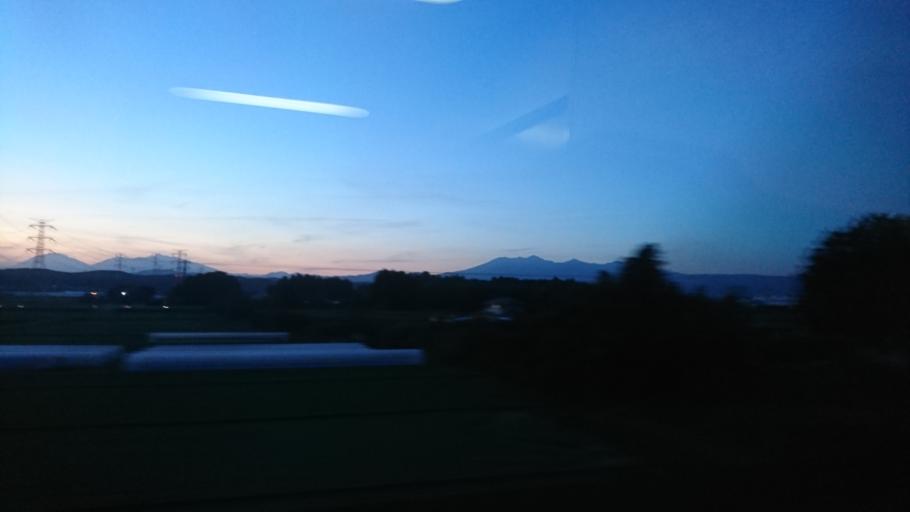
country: JP
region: Tochigi
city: Yaita
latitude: 36.7793
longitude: 139.9513
